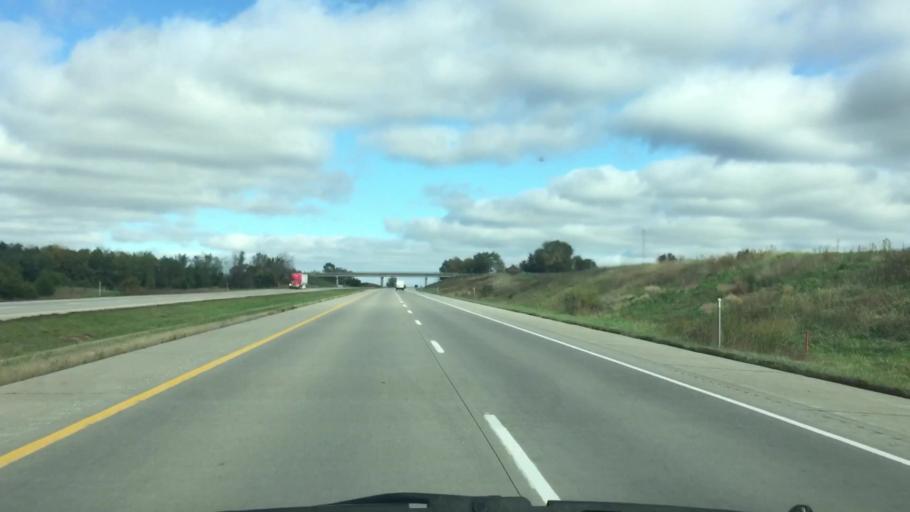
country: US
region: Iowa
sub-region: Clarke County
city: Osceola
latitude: 40.9098
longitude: -93.7967
